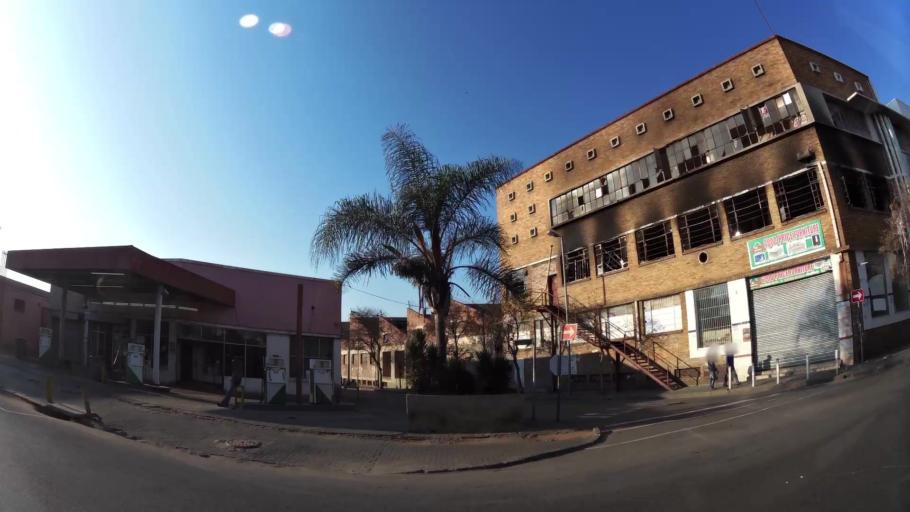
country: ZA
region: Gauteng
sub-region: Ekurhuleni Metropolitan Municipality
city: Germiston
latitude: -26.2118
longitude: 28.1652
